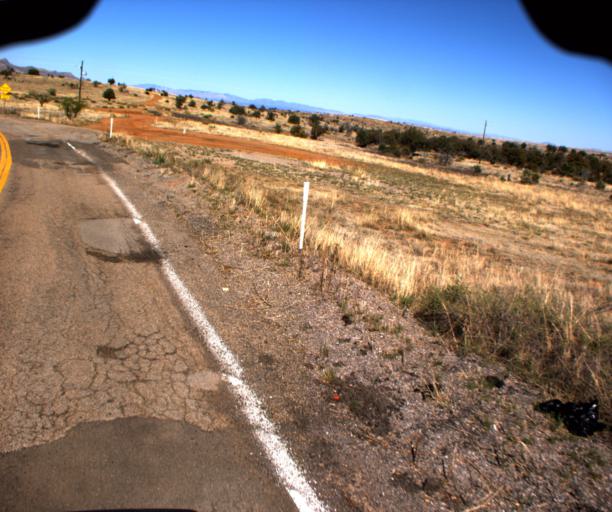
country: US
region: Arizona
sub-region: Cochise County
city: Huachuca City
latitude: 31.5746
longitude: -110.5550
